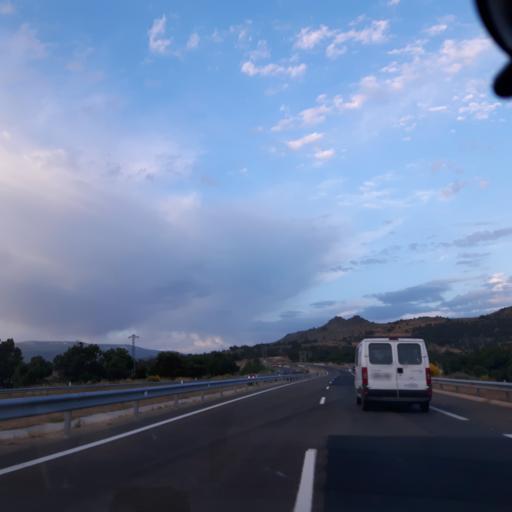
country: ES
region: Castille and Leon
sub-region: Provincia de Salamanca
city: Nava de Bejar
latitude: 40.4799
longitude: -5.6790
